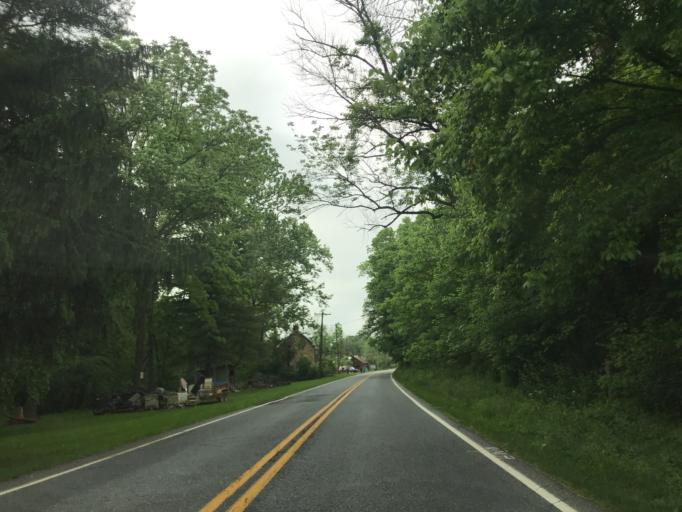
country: US
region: Maryland
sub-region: Frederick County
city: Clover Hill
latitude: 39.4961
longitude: -77.4006
